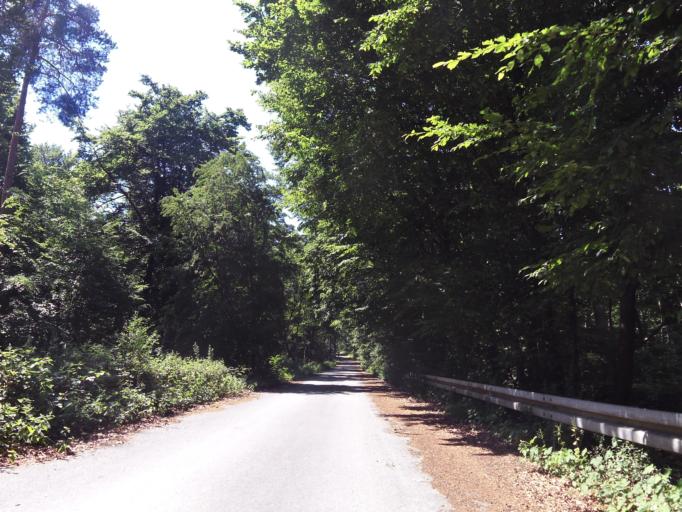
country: DE
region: Hesse
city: Morfelden-Walldorf
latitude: 49.9726
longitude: 8.6023
